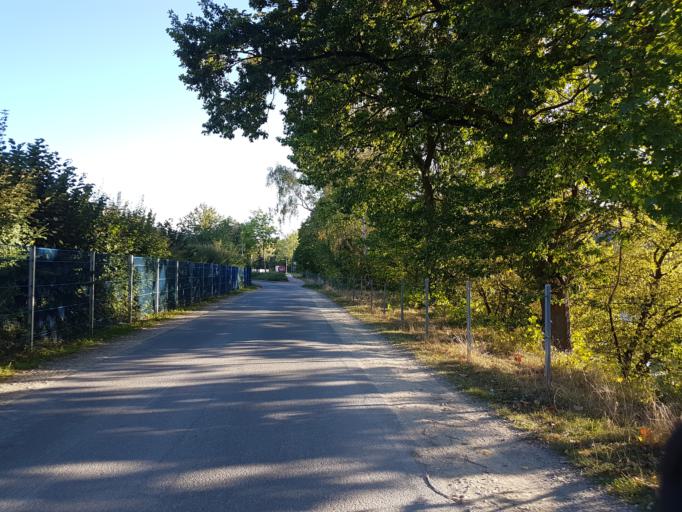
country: DE
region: North Rhine-Westphalia
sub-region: Regierungsbezirk Detmold
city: Vlotho
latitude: 52.1828
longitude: 8.8663
